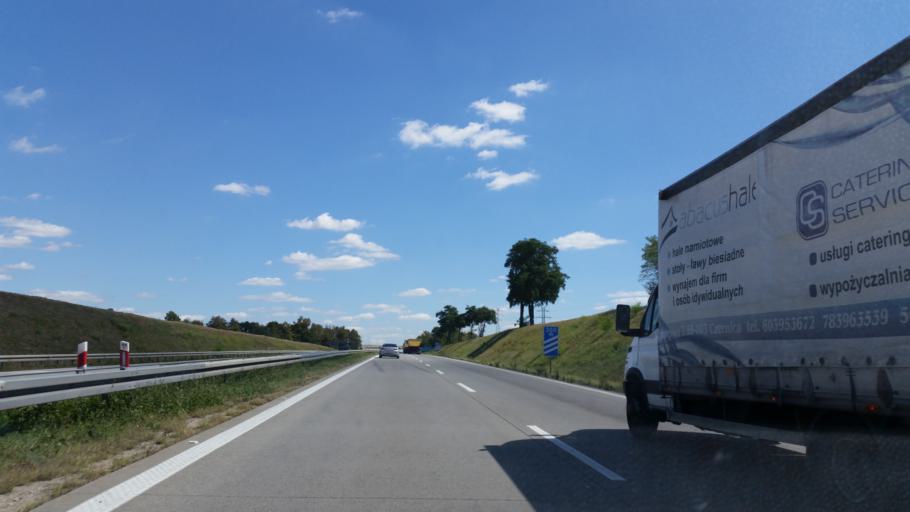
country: PL
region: Lower Silesian Voivodeship
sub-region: Powiat legnicki
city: Legnickie Pole
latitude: 51.1528
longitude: 16.2328
